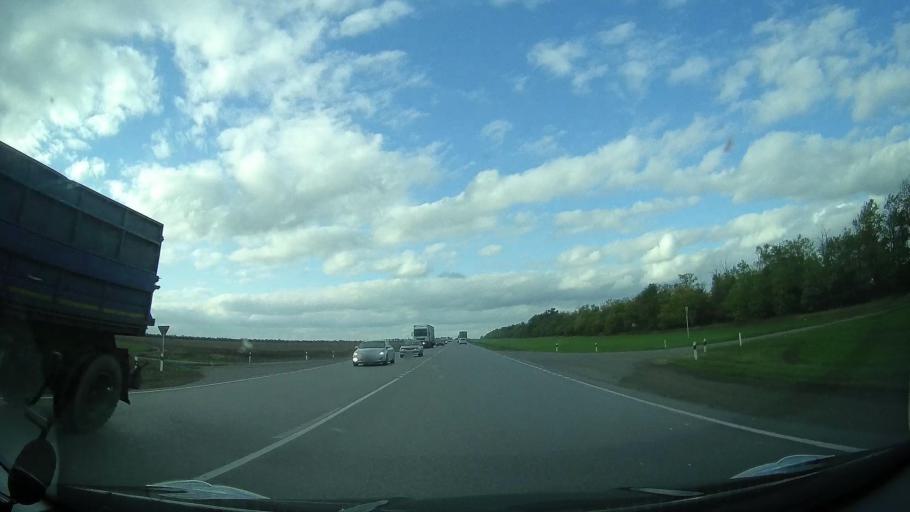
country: RU
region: Rostov
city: Kagal'nitskaya
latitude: 46.9166
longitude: 40.1083
